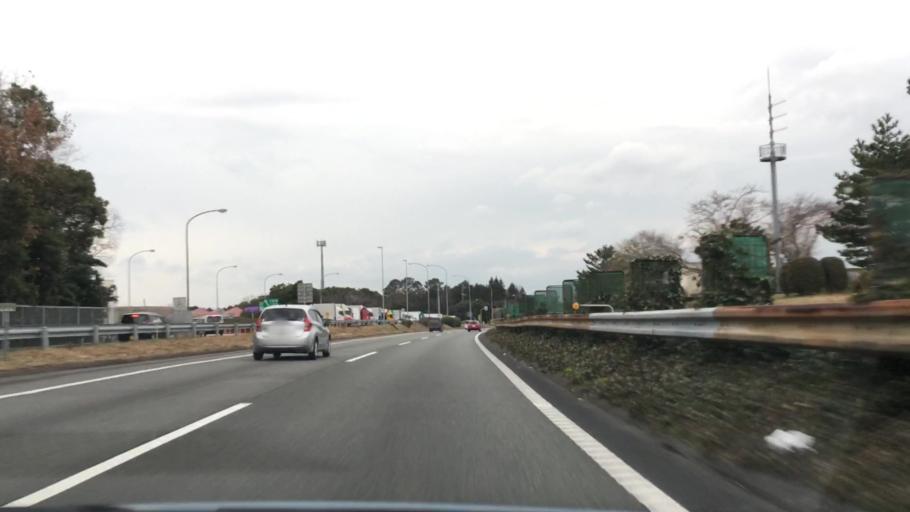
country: JP
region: Shizuoka
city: Numazu
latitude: 35.1427
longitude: 138.8386
